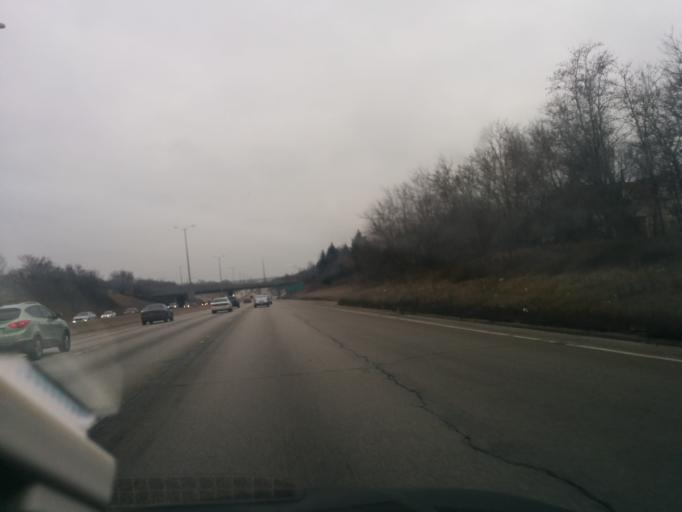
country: US
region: Wisconsin
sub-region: Milwaukee County
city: Shorewood
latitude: 43.0770
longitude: -87.9211
